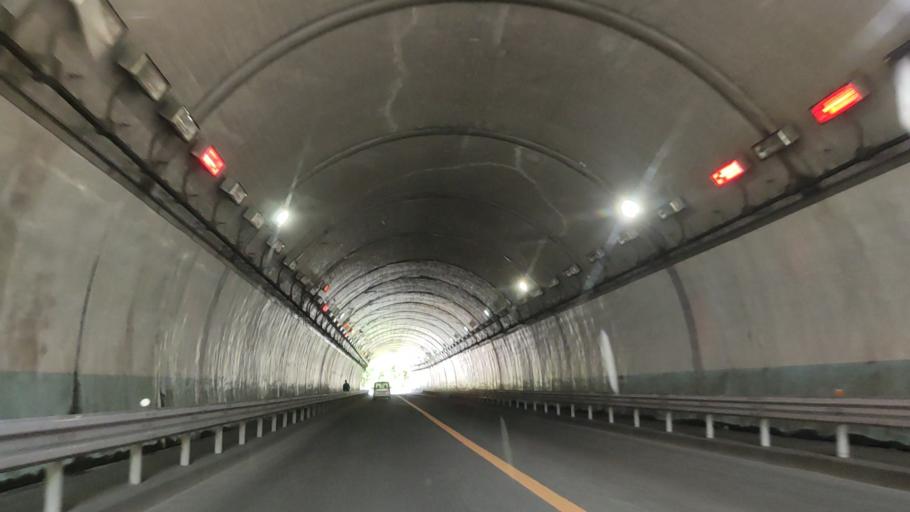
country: JP
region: Kanagawa
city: Yokohama
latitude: 35.3998
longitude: 139.6088
